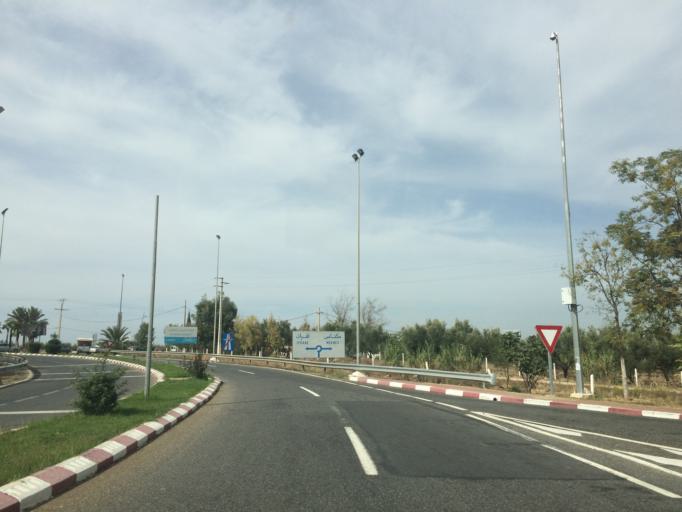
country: MA
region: Meknes-Tafilalet
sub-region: Meknes
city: Meknes
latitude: 33.8338
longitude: -5.5160
